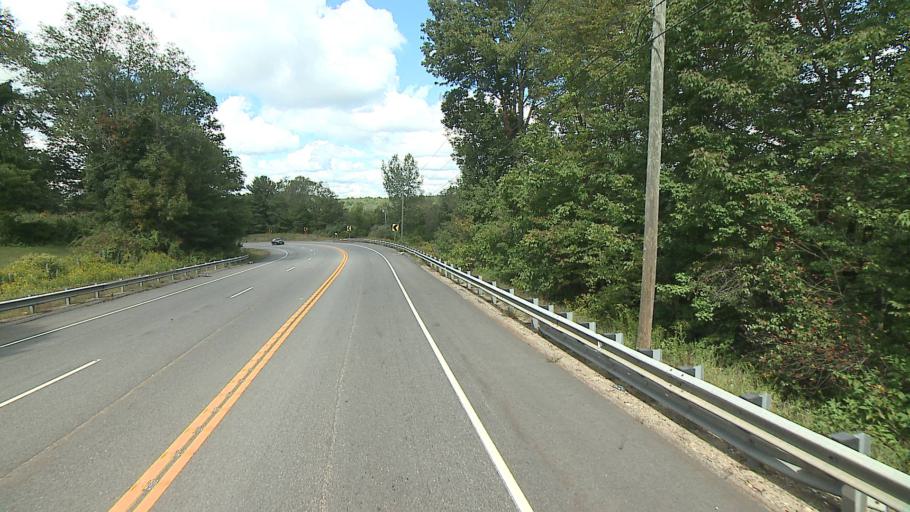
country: US
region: Connecticut
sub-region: Windham County
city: South Woodstock
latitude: 41.8782
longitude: -72.0794
